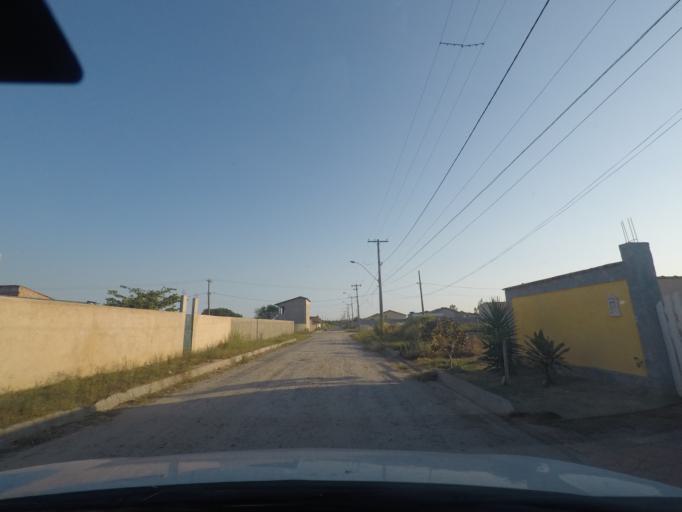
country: BR
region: Rio de Janeiro
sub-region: Marica
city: Marica
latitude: -22.9613
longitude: -42.9281
